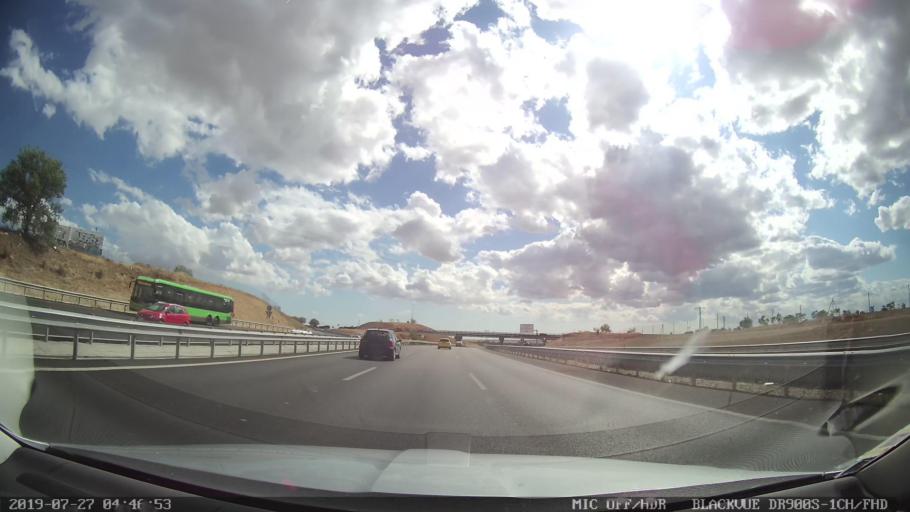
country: ES
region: Madrid
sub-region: Provincia de Madrid
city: Arroyomolinos
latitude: 40.3058
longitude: -3.9045
